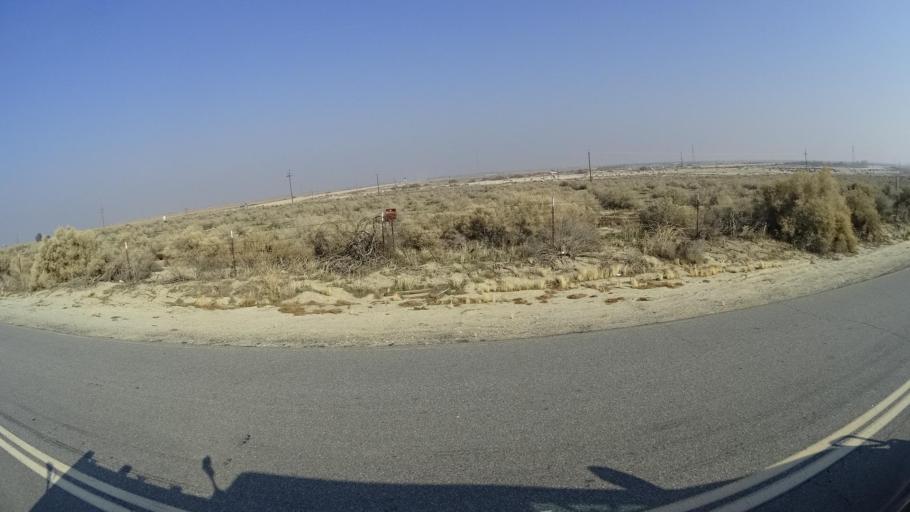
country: US
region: California
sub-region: Kern County
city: Buttonwillow
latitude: 35.2927
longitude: -119.3460
